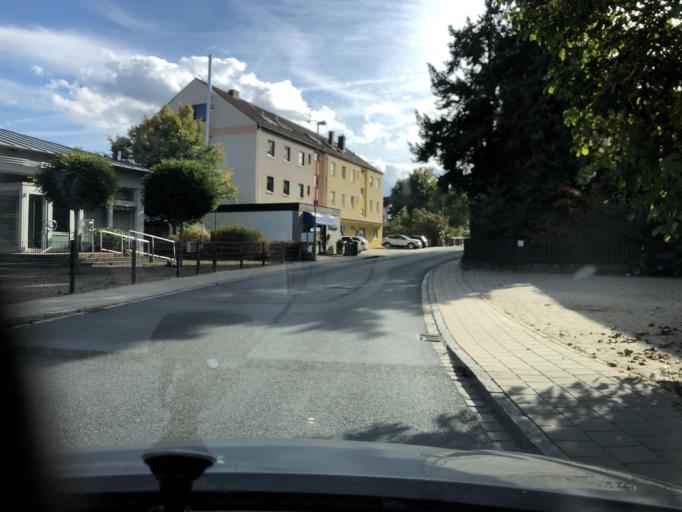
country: DE
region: Bavaria
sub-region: Regierungsbezirk Mittelfranken
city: Seukendorf
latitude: 49.4594
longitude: 10.8897
